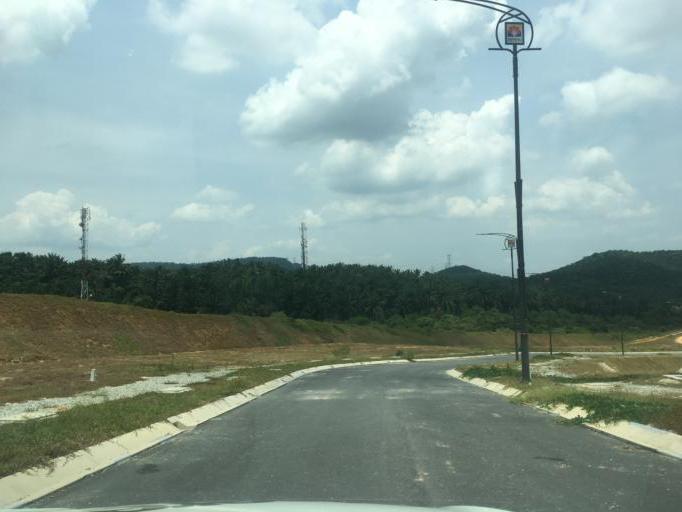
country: MY
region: Putrajaya
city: Putrajaya
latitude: 2.8486
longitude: 101.7099
